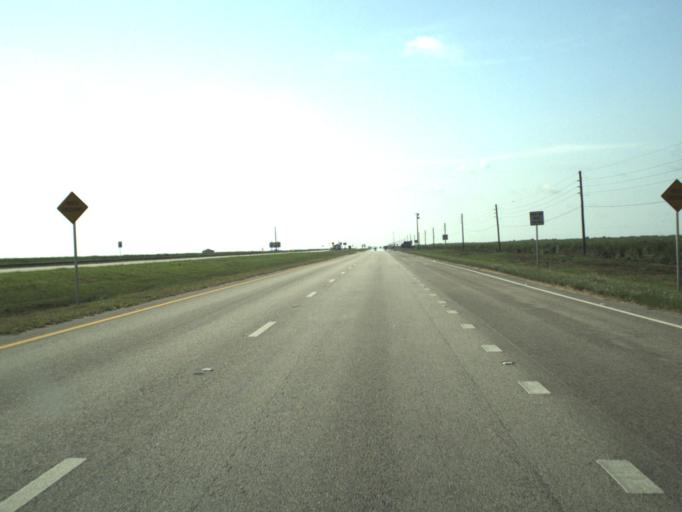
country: US
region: Florida
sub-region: Palm Beach County
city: Belle Glade Camp
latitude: 26.5437
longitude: -80.6999
